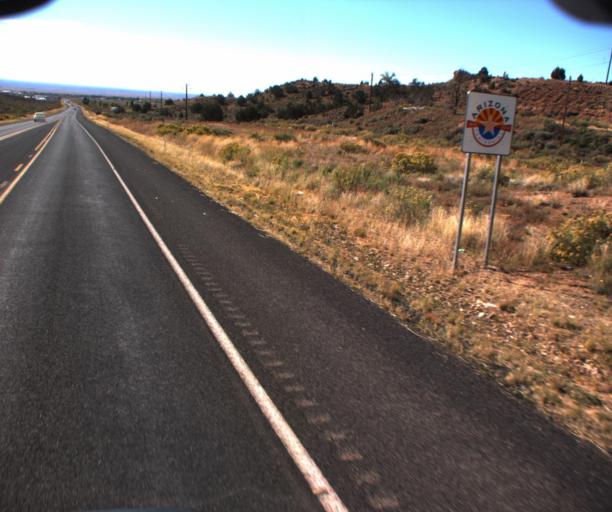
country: US
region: Arizona
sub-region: Coconino County
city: Fredonia
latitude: 36.9880
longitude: -112.5303
